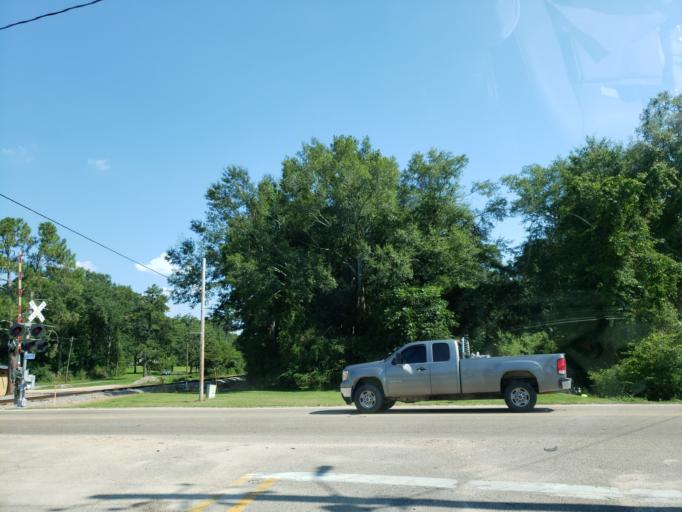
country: US
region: Mississippi
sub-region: Covington County
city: Collins
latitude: 31.5619
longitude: -89.4972
